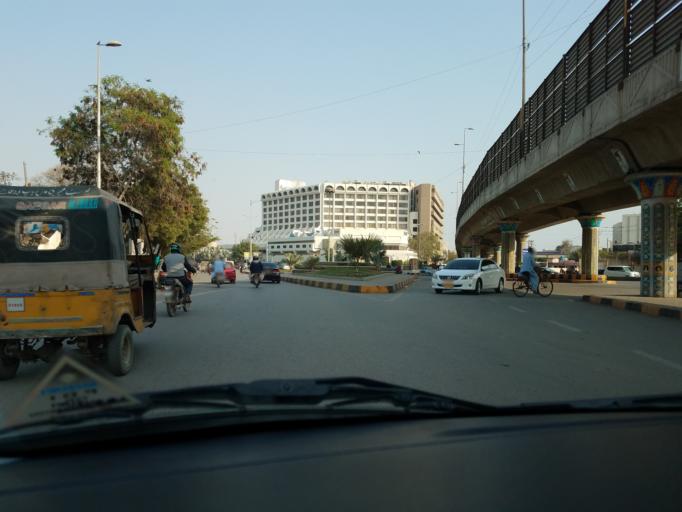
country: PK
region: Sindh
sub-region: Karachi District
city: Karachi
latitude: 24.8557
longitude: 67.0377
